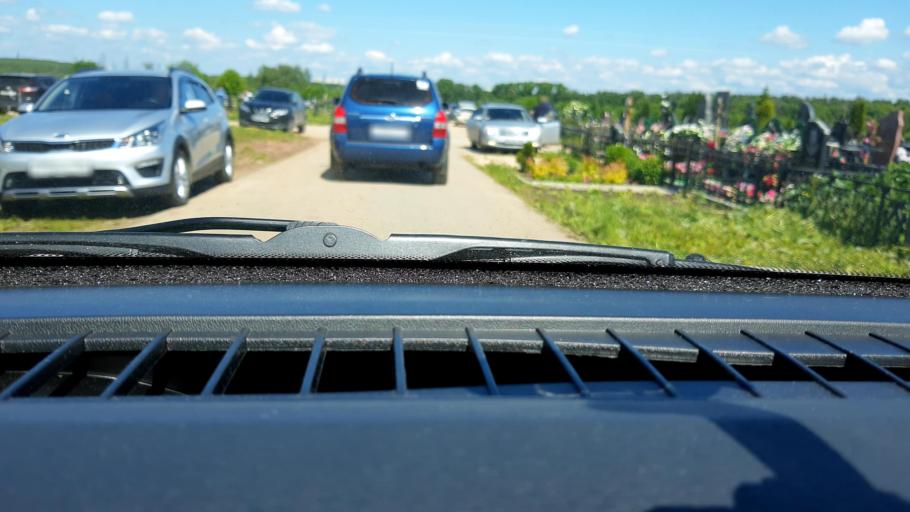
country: RU
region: Nizjnij Novgorod
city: Afonino
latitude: 56.2294
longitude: 44.0775
